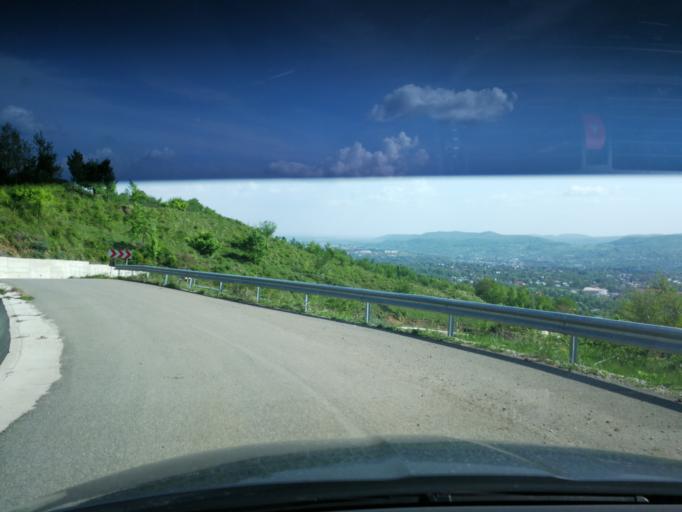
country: RO
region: Prahova
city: Cornu de Sus
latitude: 45.1720
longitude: 25.7072
